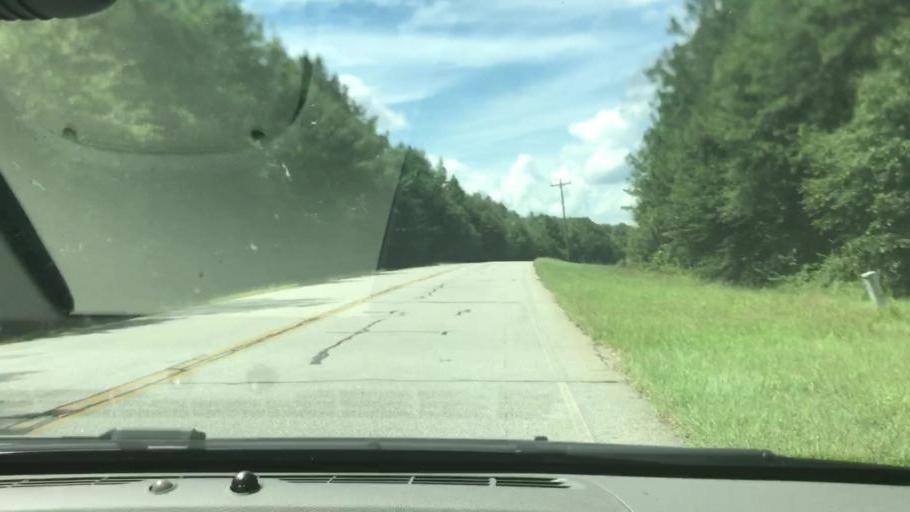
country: US
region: Georgia
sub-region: Stewart County
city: Lumpkin
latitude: 32.1380
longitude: -84.9457
